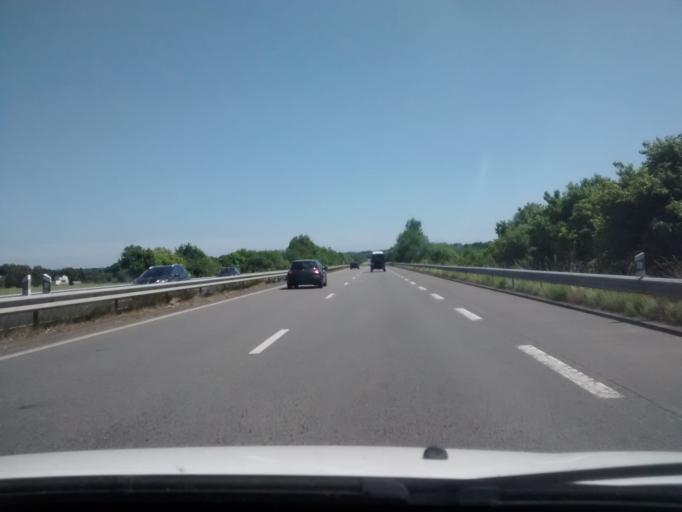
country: FR
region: Brittany
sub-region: Departement d'Ille-et-Vilaine
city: Pleugueneuc
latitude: 48.3860
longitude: -1.9026
